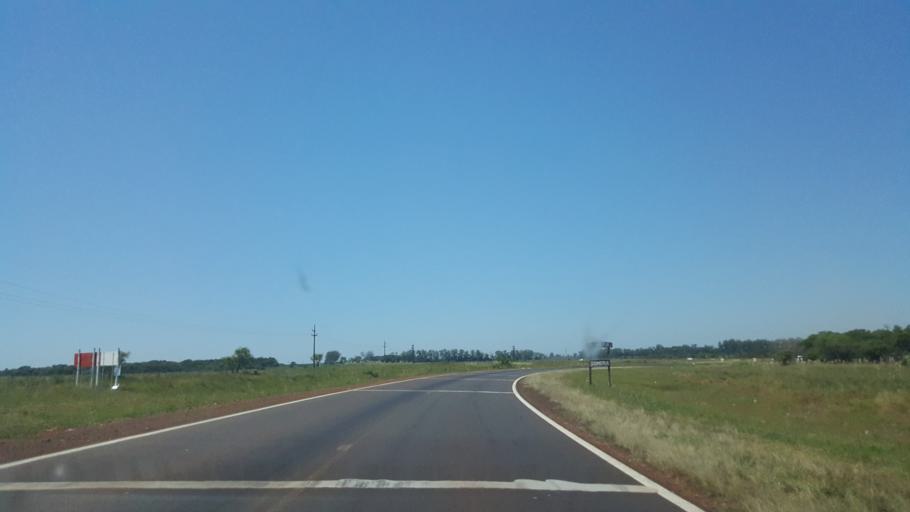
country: AR
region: Corrientes
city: Santo Tome
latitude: -28.3548
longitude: -56.1103
